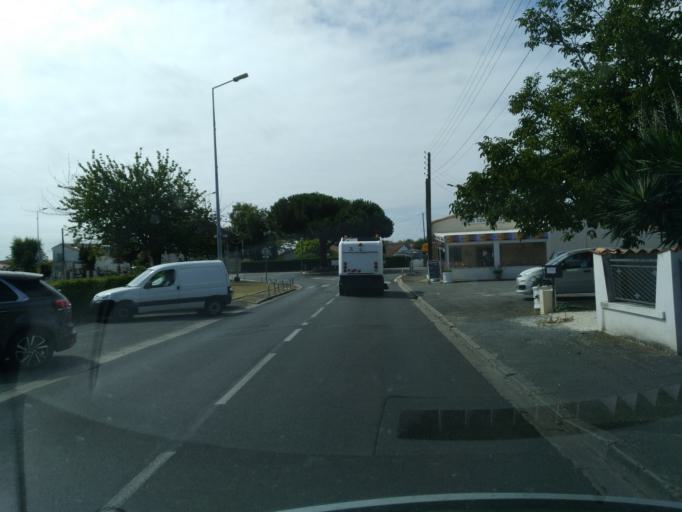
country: FR
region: Poitou-Charentes
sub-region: Departement de la Charente-Maritime
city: Saint-Palais-sur-Mer
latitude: 45.6537
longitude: -1.0785
